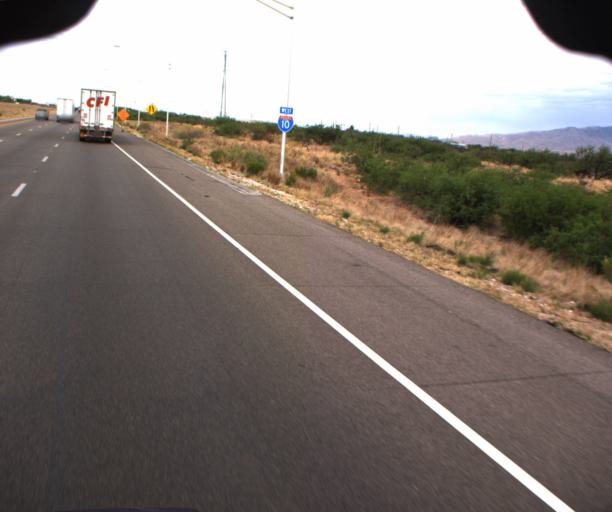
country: US
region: Arizona
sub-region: Cochise County
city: Whetstone
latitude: 31.9635
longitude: -110.3604
